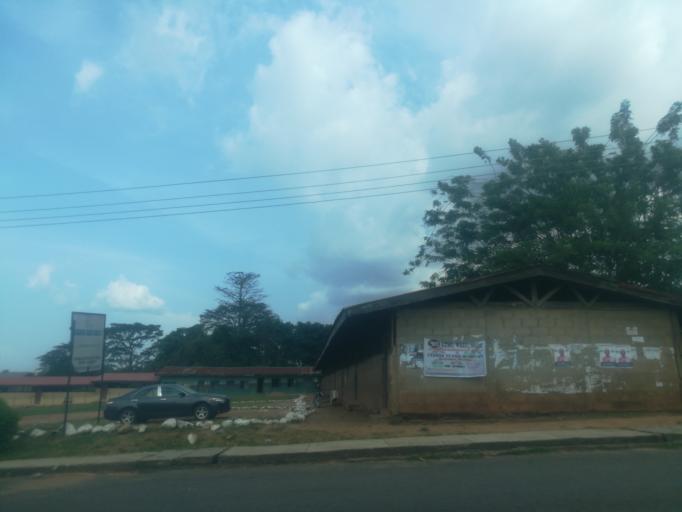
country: NG
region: Oyo
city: Moniya
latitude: 7.4548
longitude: 3.8989
